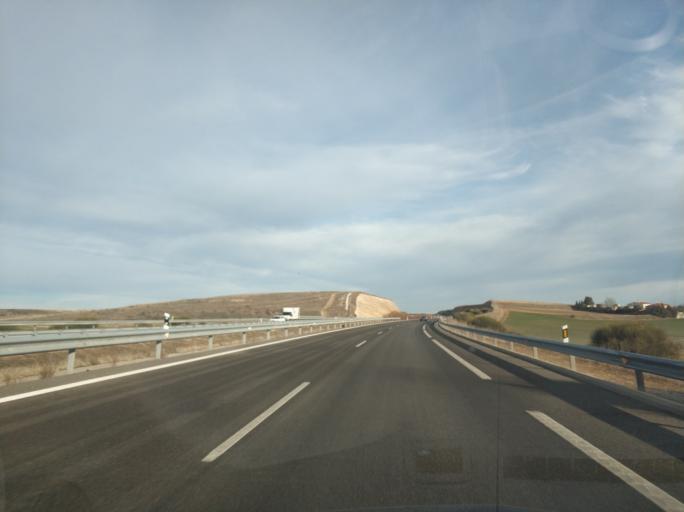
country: ES
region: Castille and Leon
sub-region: Provincia de Salamanca
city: Villamayor
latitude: 41.0074
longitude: -5.6793
